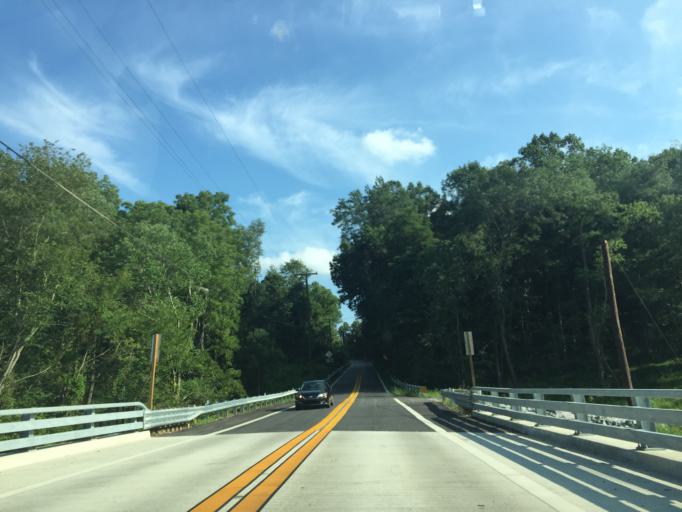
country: US
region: Maryland
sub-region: Carroll County
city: Hampstead
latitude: 39.6156
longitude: -76.7902
